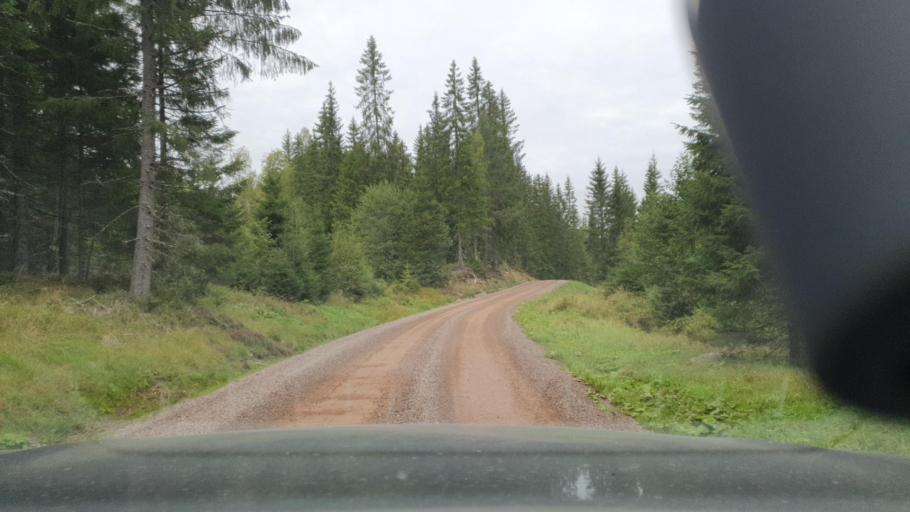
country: SE
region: Vaermland
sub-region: Eda Kommun
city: Charlottenberg
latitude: 60.0429
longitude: 12.5758
